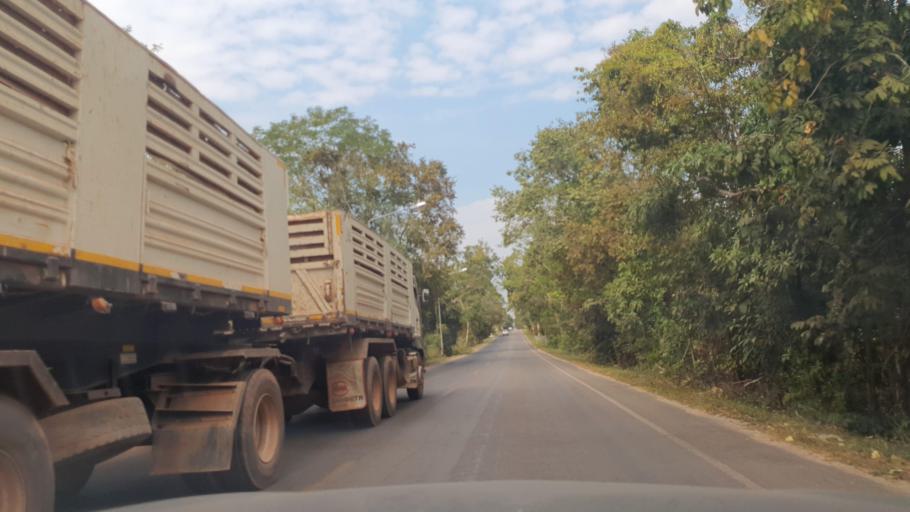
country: TH
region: Changwat Bueng Kan
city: Si Wilai
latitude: 18.2820
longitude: 103.8282
